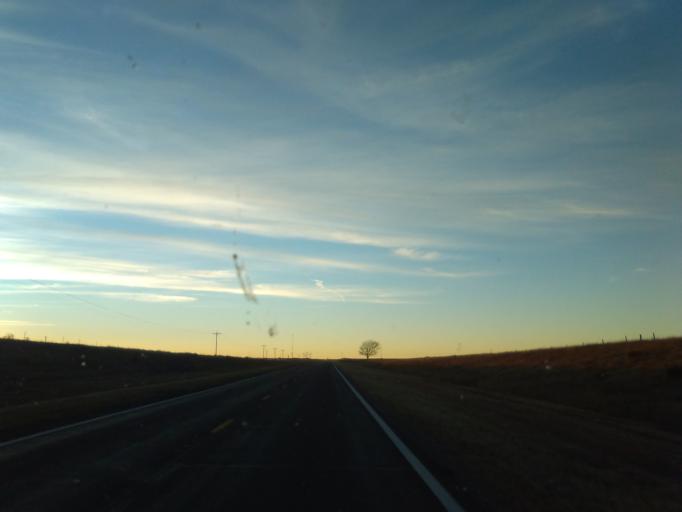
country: US
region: Kansas
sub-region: Wallace County
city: Sharon Springs
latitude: 38.9021
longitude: -101.7072
